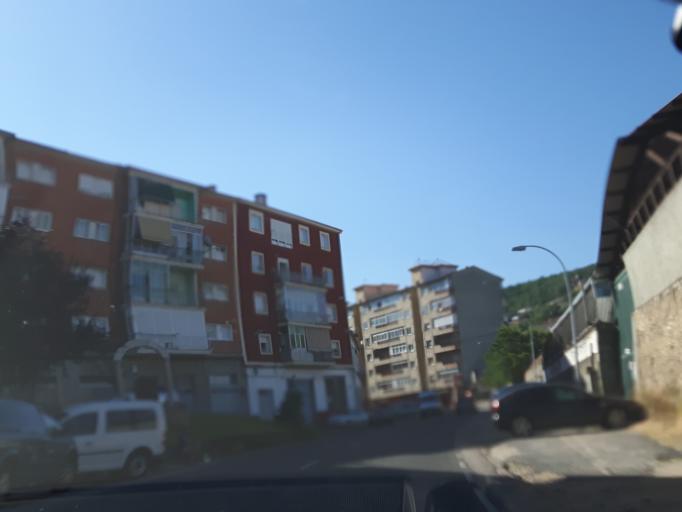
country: ES
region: Castille and Leon
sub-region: Provincia de Salamanca
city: Bejar
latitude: 40.3880
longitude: -5.7610
